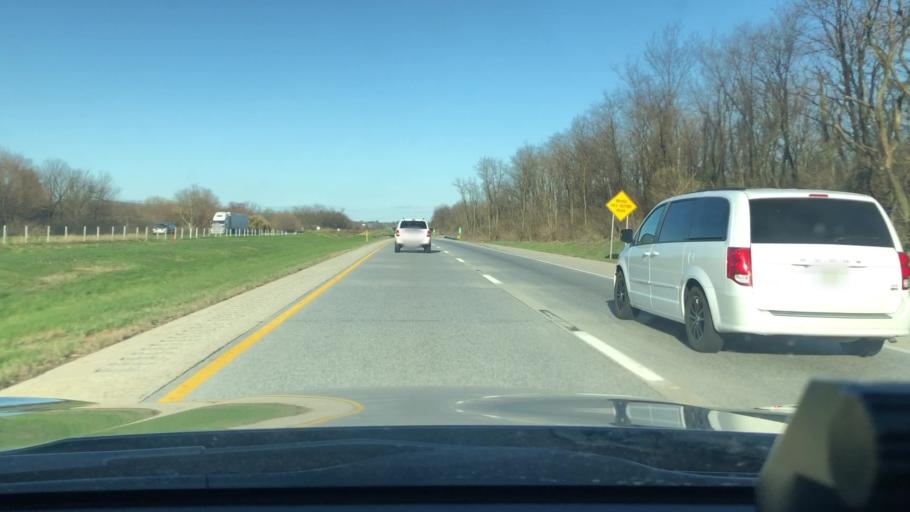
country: US
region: Pennsylvania
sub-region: Lebanon County
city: Fredericksburg
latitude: 40.4496
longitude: -76.4487
